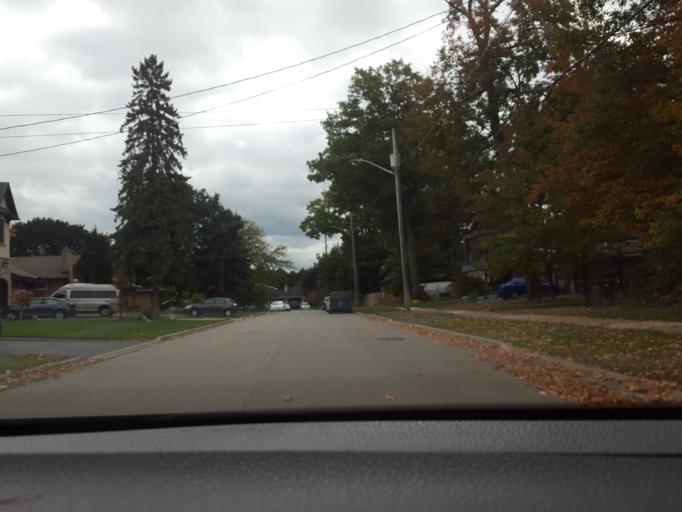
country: CA
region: Ontario
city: Mississauga
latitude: 43.5774
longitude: -79.5975
